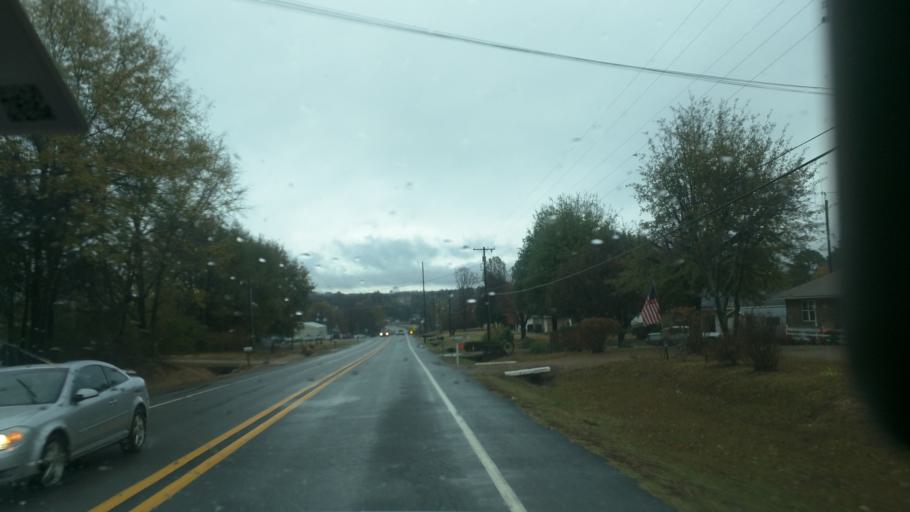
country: US
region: Arkansas
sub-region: Franklin County
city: Ozark
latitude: 35.4944
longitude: -93.8436
